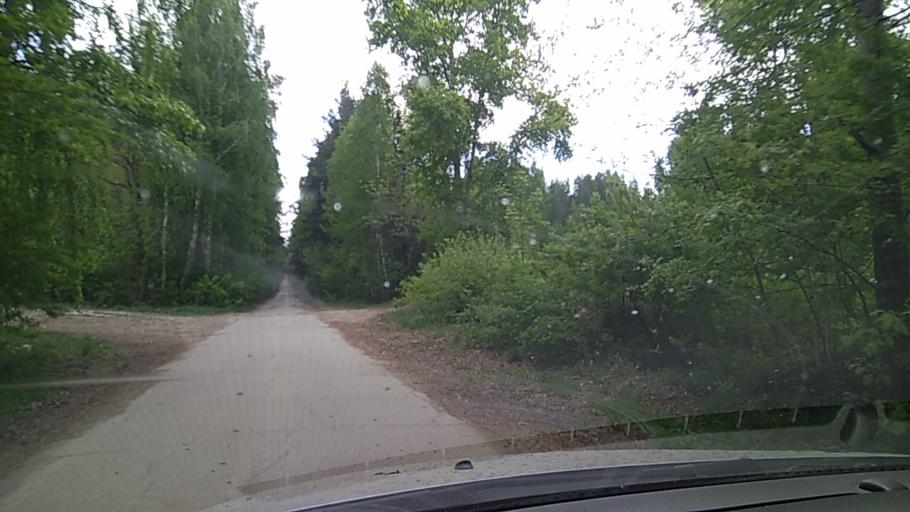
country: RU
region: Sverdlovsk
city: Verkhnyaya Pyshma
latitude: 56.9257
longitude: 60.6013
